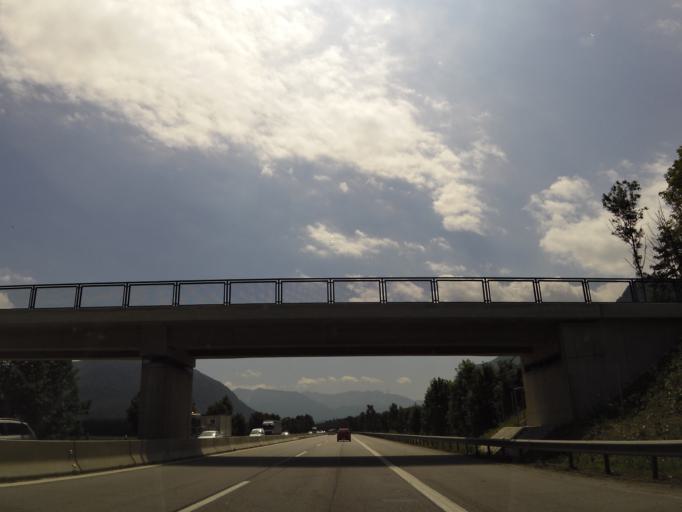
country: DE
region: Bavaria
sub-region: Upper Bavaria
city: Flintsbach
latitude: 47.7296
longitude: 12.1341
